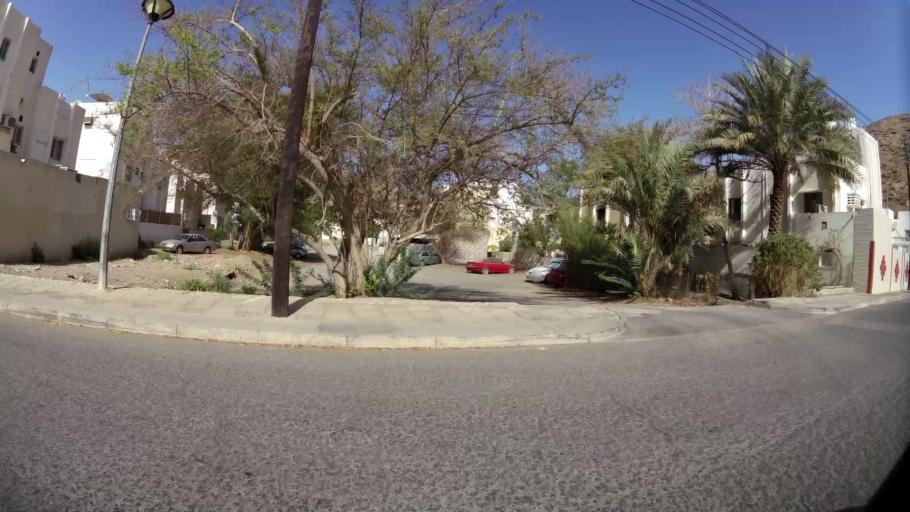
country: OM
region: Muhafazat Masqat
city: Muscat
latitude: 23.6014
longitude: 58.5114
